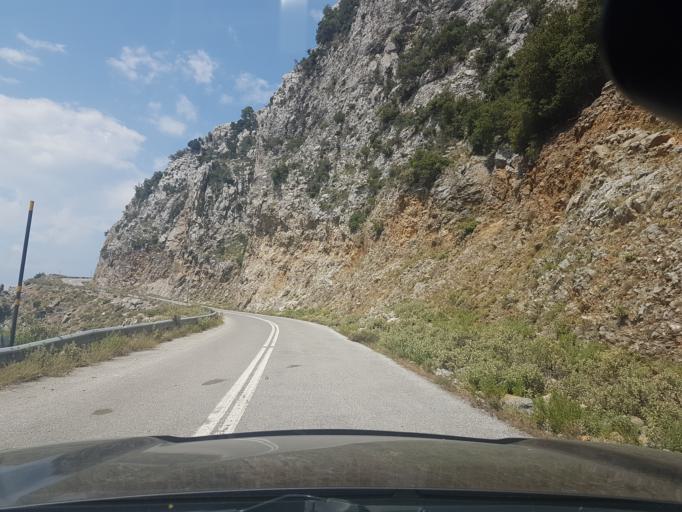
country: GR
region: Central Greece
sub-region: Nomos Evvoias
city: Kymi
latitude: 38.6535
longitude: 23.9674
